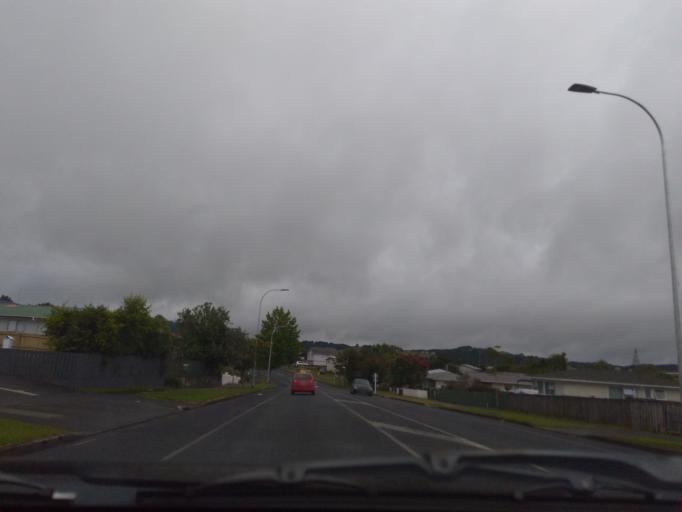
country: NZ
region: Northland
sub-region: Whangarei
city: Whangarei
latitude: -35.6854
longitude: 174.3260
